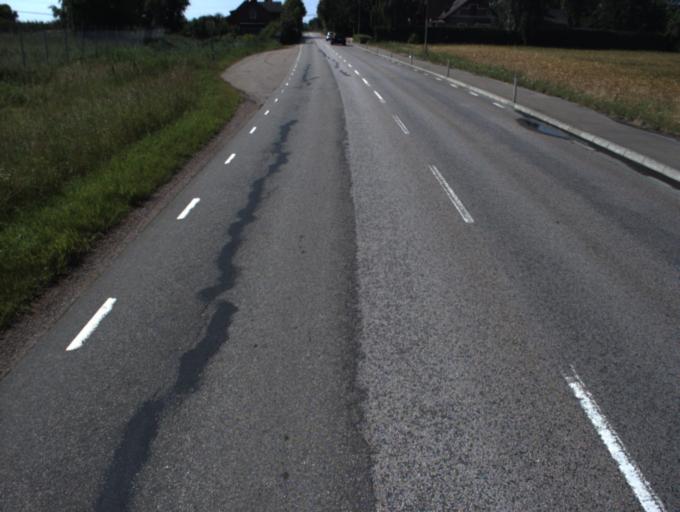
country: SE
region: Skane
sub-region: Angelholms Kommun
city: Strovelstorp
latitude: 56.1328
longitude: 12.8104
